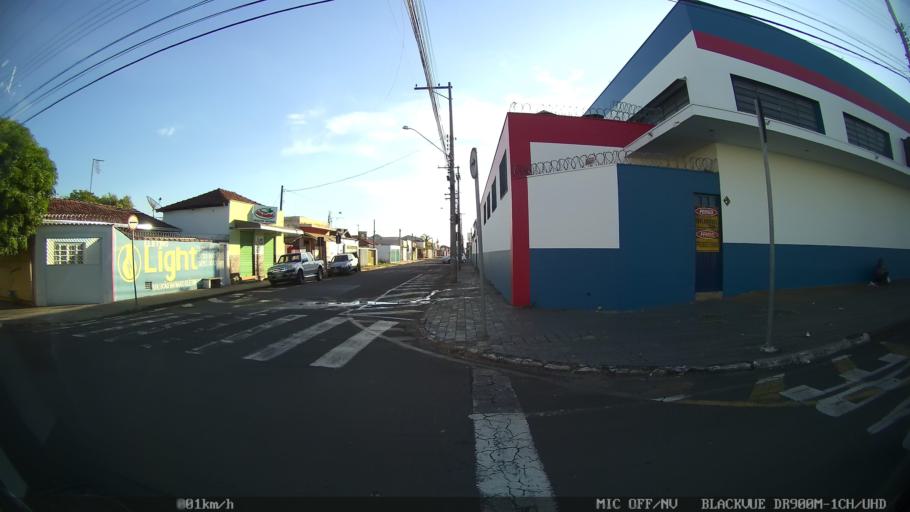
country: BR
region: Sao Paulo
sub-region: Franca
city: Franca
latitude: -20.5272
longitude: -47.3767
